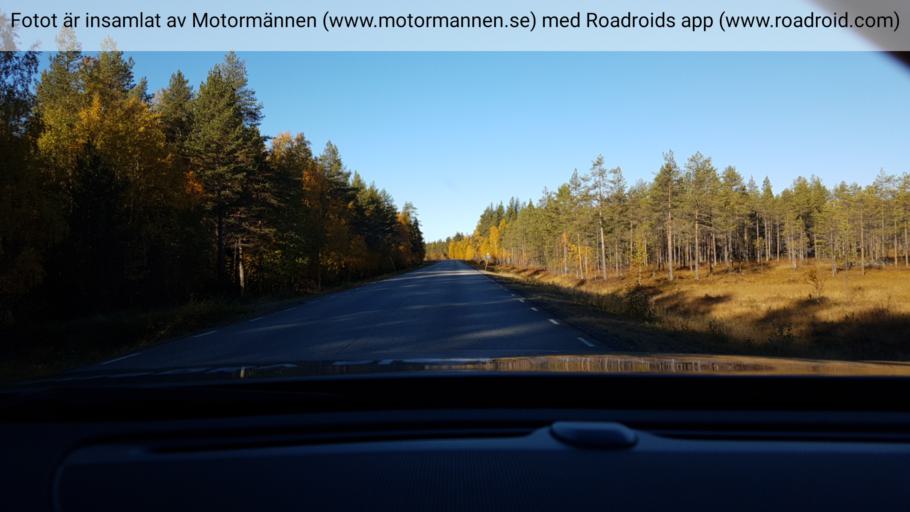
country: SE
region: Norrbotten
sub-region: Pitea Kommun
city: Roknas
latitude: 65.3421
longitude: 20.9600
